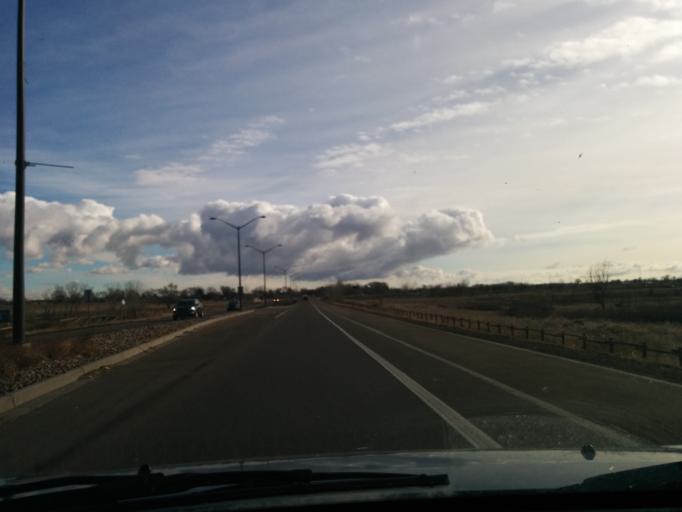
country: US
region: Colorado
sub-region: Larimer County
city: Fort Collins
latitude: 40.5669
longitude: -105.0234
